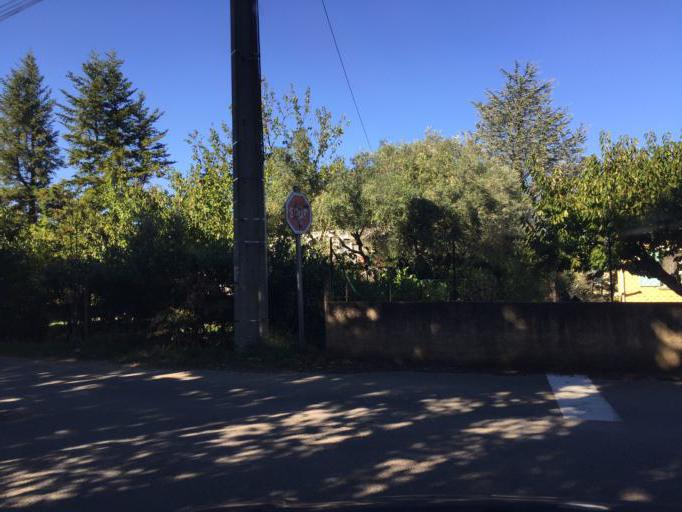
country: FR
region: Provence-Alpes-Cote d'Azur
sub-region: Departement du Vaucluse
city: Piolenc
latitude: 44.1757
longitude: 4.7719
